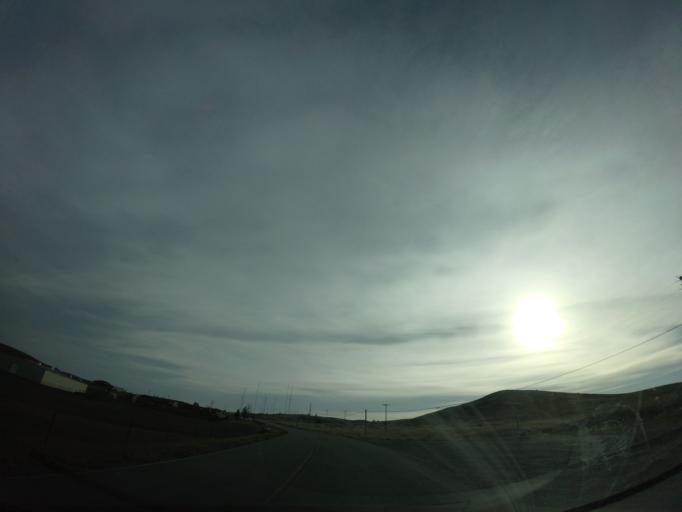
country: US
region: Montana
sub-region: Yellowstone County
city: Billings
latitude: 45.7765
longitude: -108.4626
